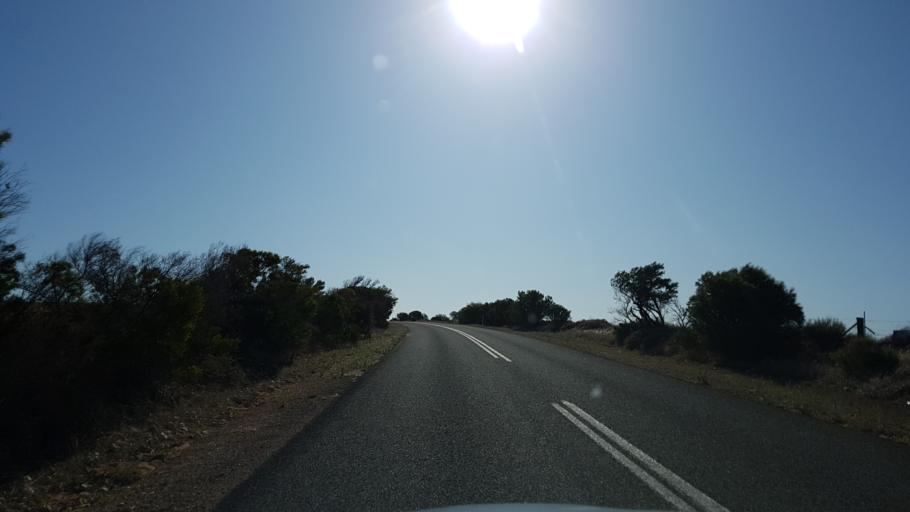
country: AU
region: South Australia
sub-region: Mid Murray
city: Mannum
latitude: -34.7751
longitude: 139.5442
